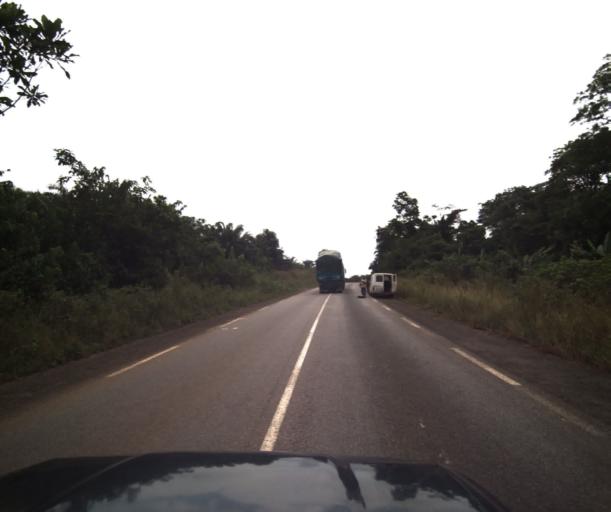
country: CM
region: Littoral
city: Edea
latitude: 3.8272
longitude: 10.3915
